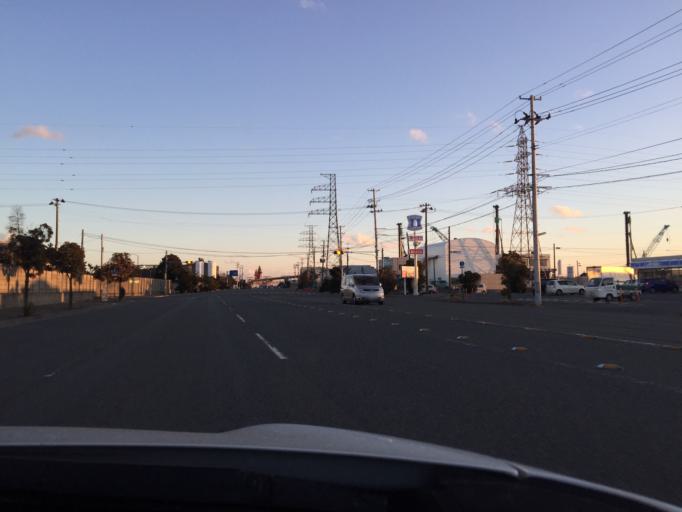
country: JP
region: Fukushima
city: Iwaki
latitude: 36.9419
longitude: 140.8759
